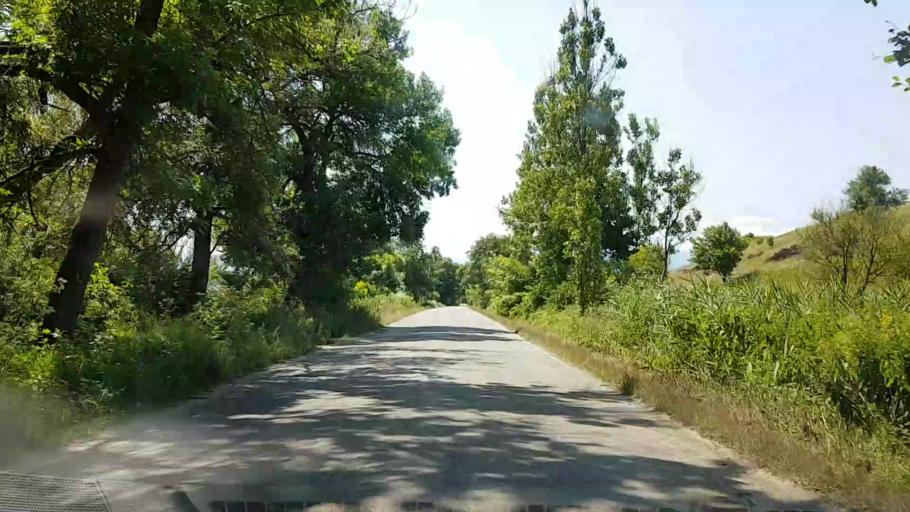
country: RO
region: Brasov
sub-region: Comuna Voila
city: Voila
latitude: 45.8485
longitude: 24.8326
